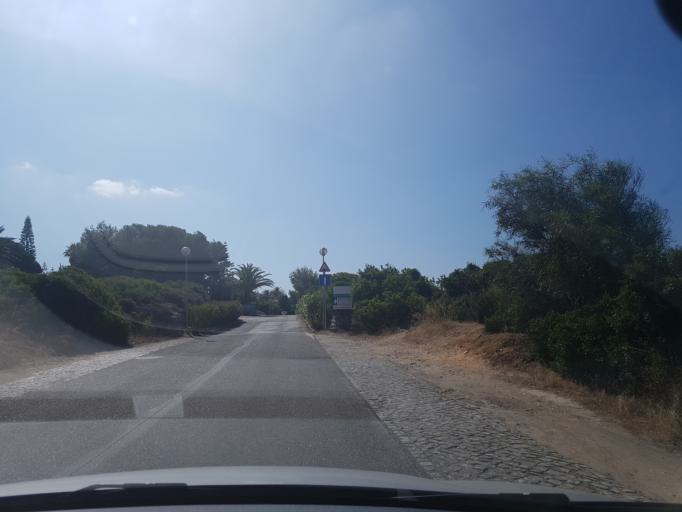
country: PT
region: Faro
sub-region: Lagoa
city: Carvoeiro
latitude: 37.0878
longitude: -8.4376
